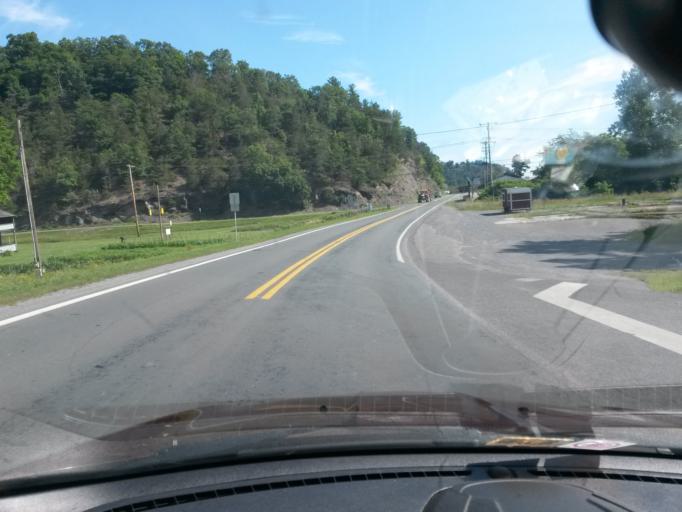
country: US
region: Virginia
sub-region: Shenandoah County
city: Basye
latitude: 38.8769
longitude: -78.8666
